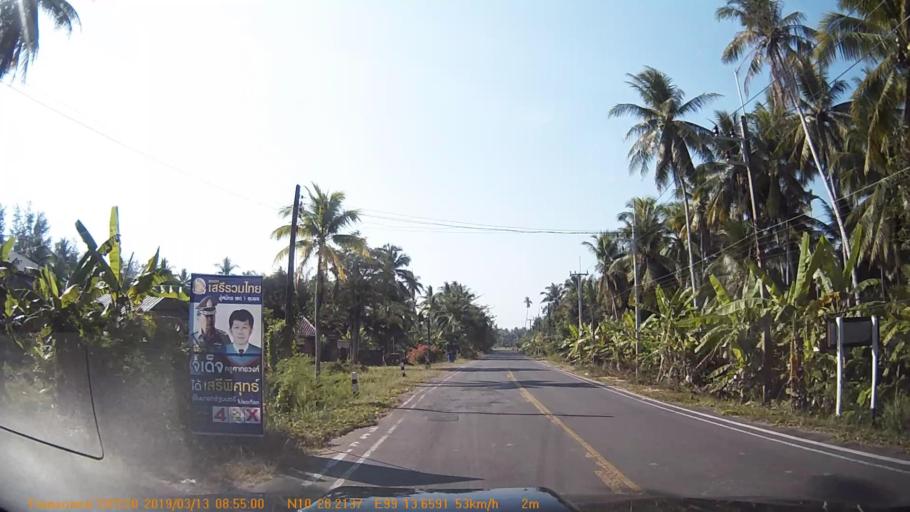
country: TH
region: Chumphon
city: Chumphon
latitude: 10.4701
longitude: 99.2277
